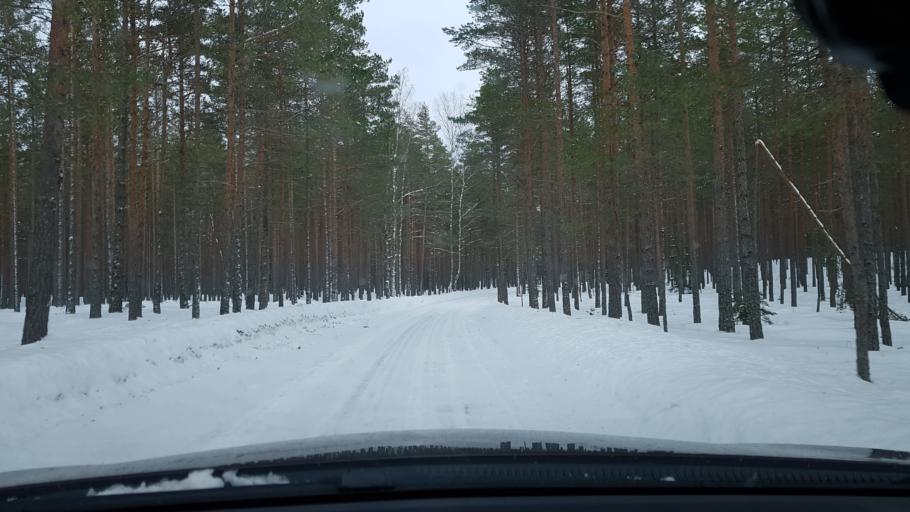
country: EE
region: Laeaene-Virumaa
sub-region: Kadrina vald
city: Kadrina
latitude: 59.5576
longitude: 26.0224
